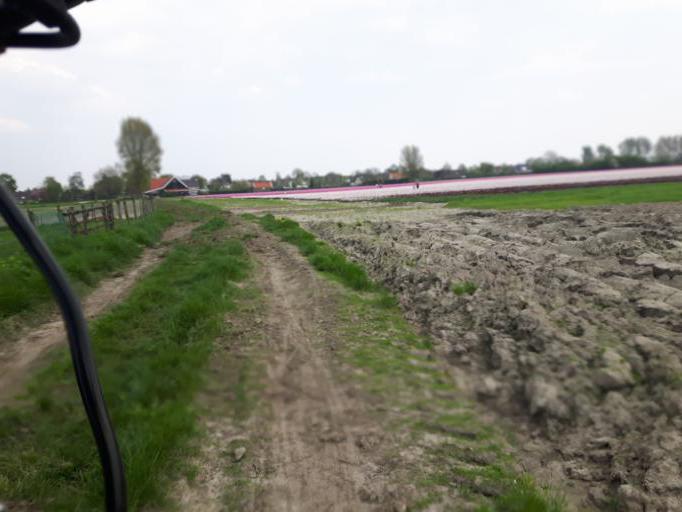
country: NL
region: Zeeland
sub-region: Gemeente Borsele
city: Borssele
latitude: 51.4676
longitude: 3.8022
